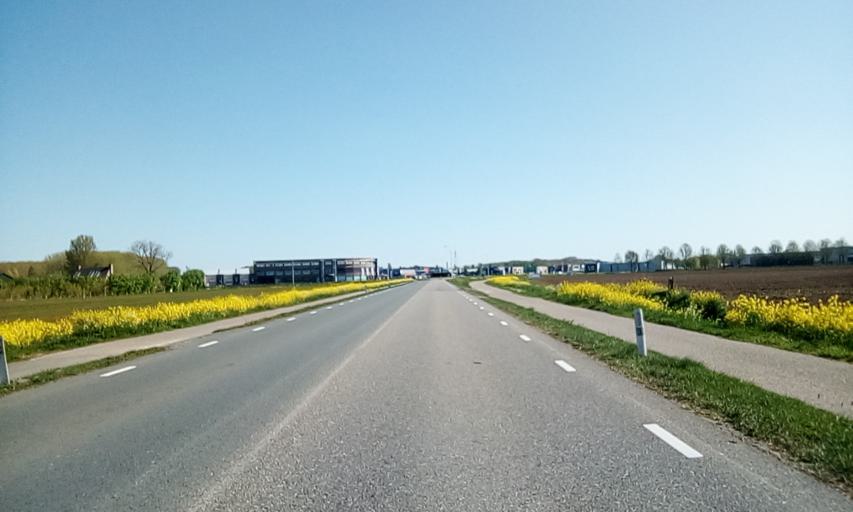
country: NL
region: Gelderland
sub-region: Gemeente Druten
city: Druten
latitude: 51.8810
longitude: 5.5694
